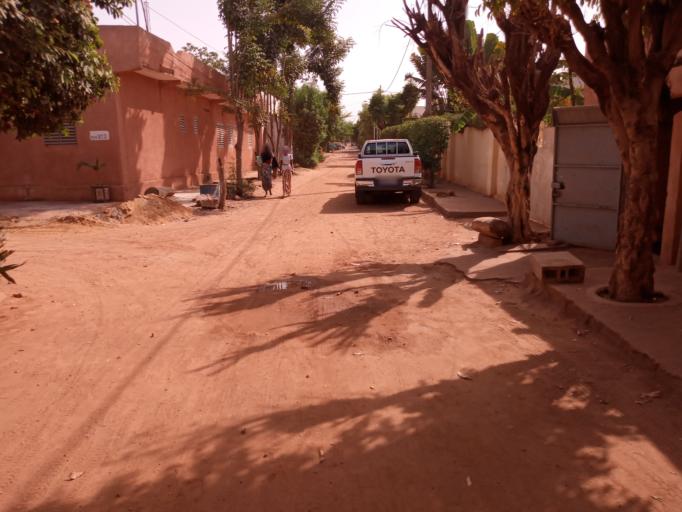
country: ML
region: Bamako
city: Bamako
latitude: 12.5867
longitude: -7.9503
